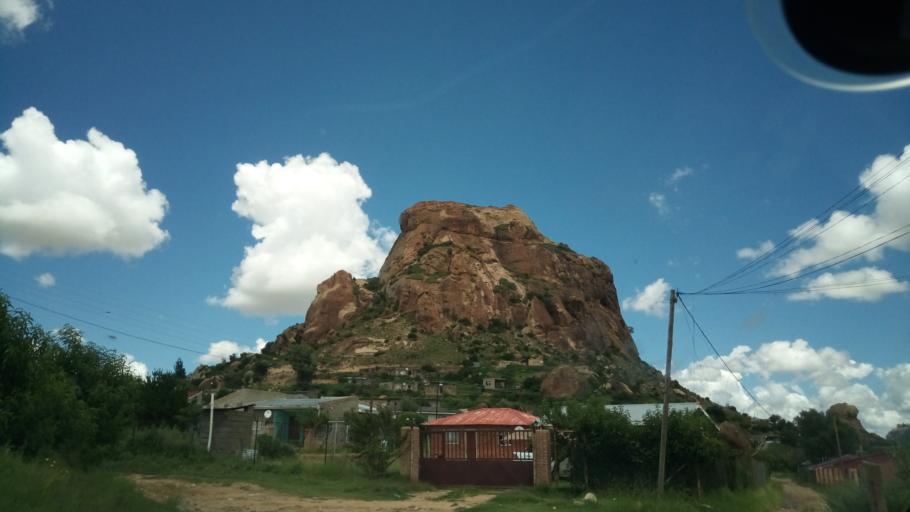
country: LS
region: Maseru
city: Maseru
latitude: -29.3509
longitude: 27.5347
